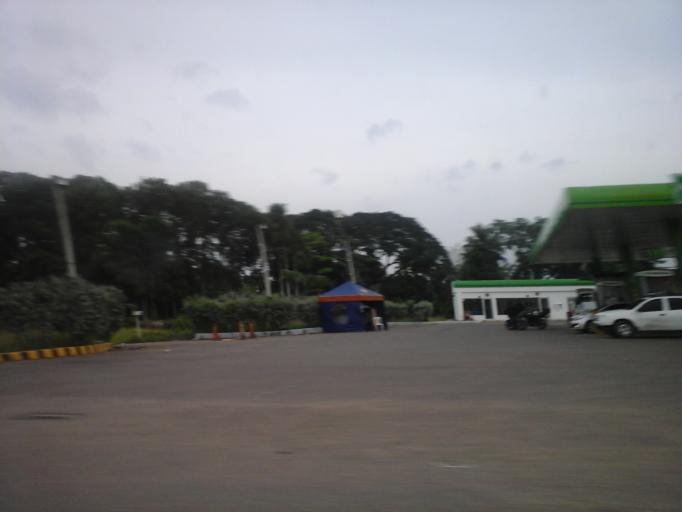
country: CO
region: Bolivar
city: San Pablo
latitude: 10.1366
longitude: -75.2702
